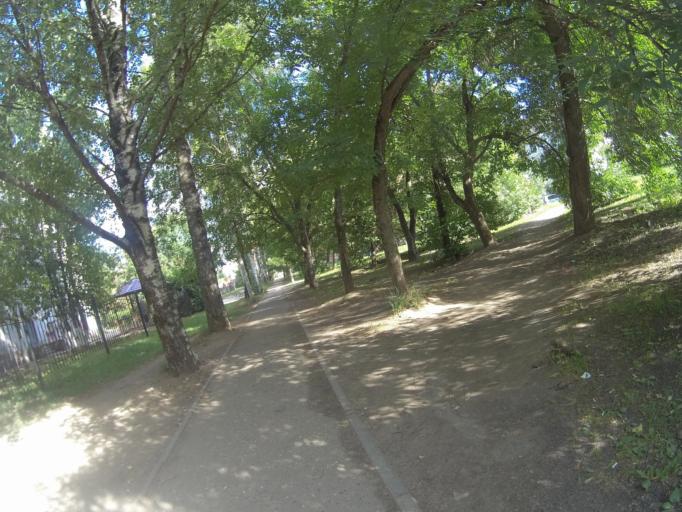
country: RU
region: Vladimir
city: Vladimir
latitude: 56.1371
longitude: 40.3631
